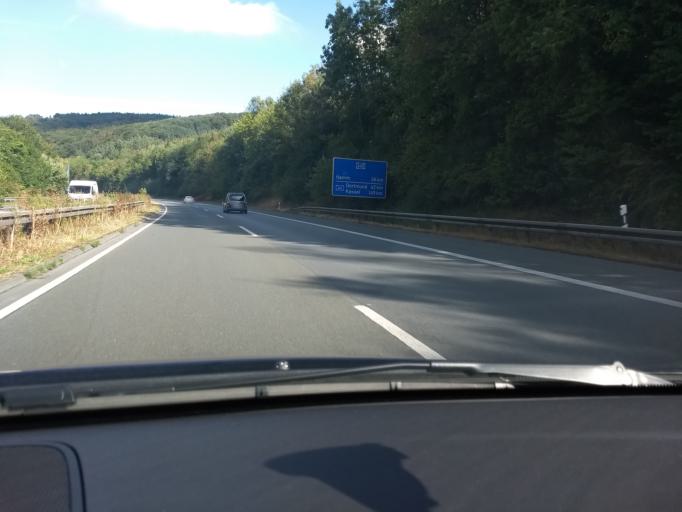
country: DE
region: North Rhine-Westphalia
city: Wickede
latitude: 51.4647
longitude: 7.9562
